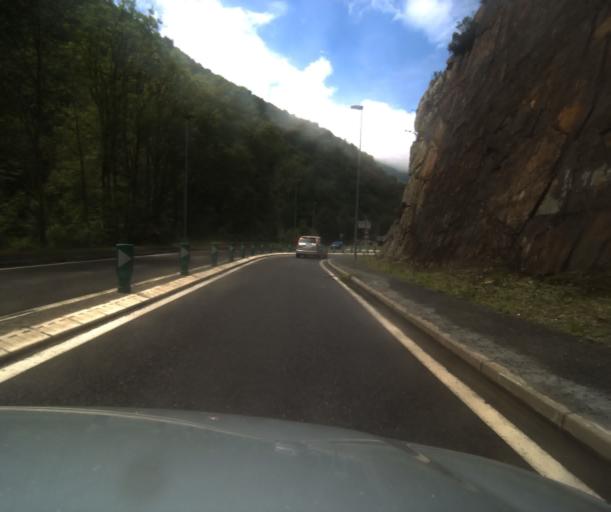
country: FR
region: Midi-Pyrenees
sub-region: Departement des Hautes-Pyrenees
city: Pierrefitte-Nestalas
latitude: 42.9505
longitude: -0.0670
